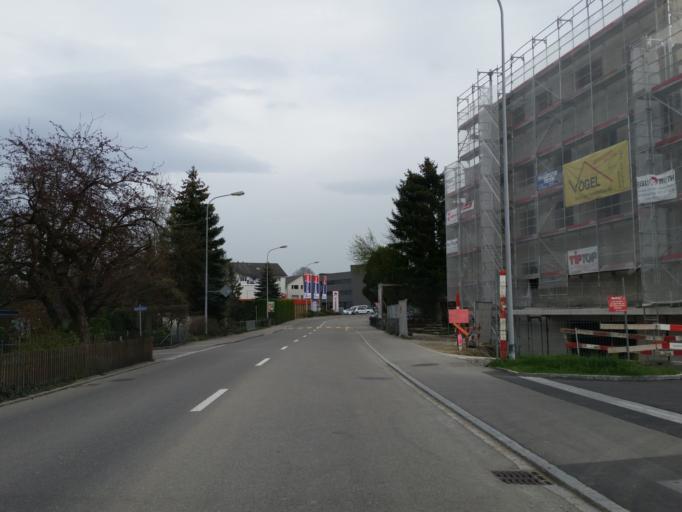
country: CH
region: Thurgau
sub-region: Arbon District
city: Amriswil
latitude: 47.5462
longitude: 9.2813
